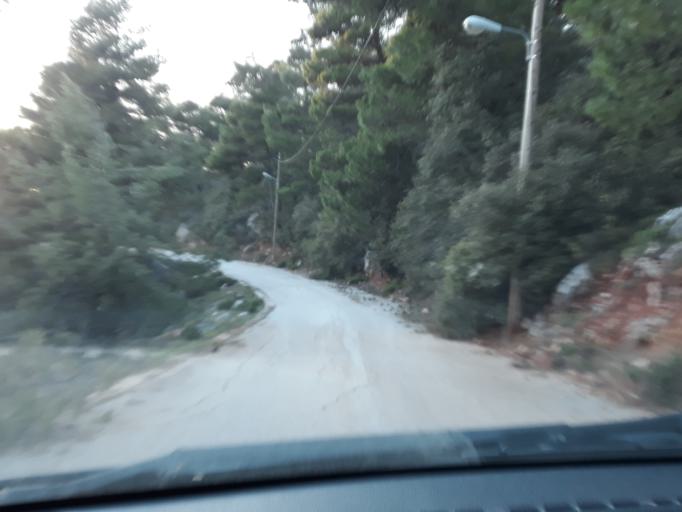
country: GR
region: Attica
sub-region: Nomarchia Anatolikis Attikis
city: Afidnes
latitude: 38.2146
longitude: 23.8103
